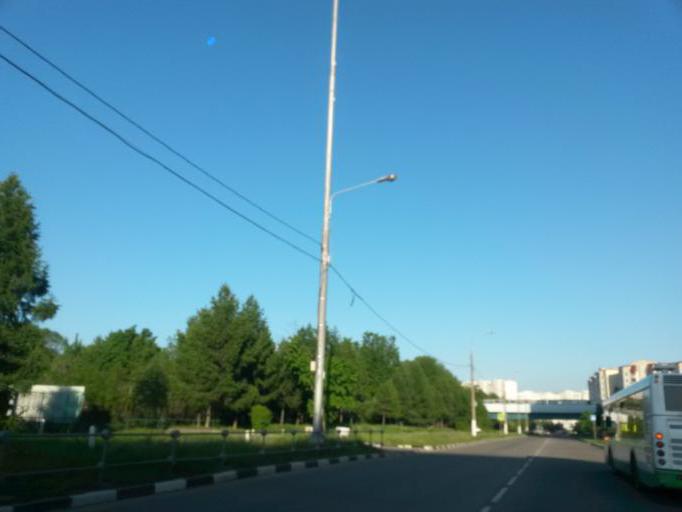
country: RU
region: Moscow
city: Annino
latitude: 55.5525
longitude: 37.5609
